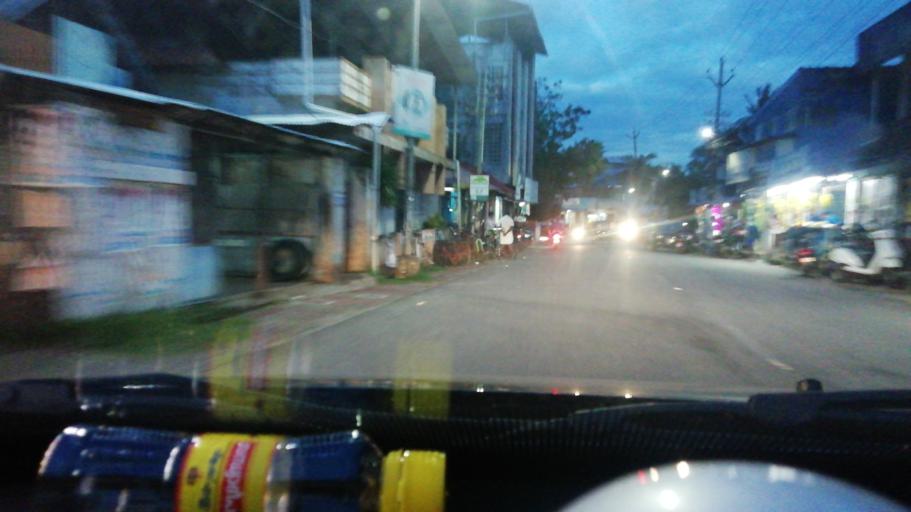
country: IN
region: Kerala
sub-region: Thiruvananthapuram
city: Paravur
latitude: 8.8108
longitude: 76.6721
